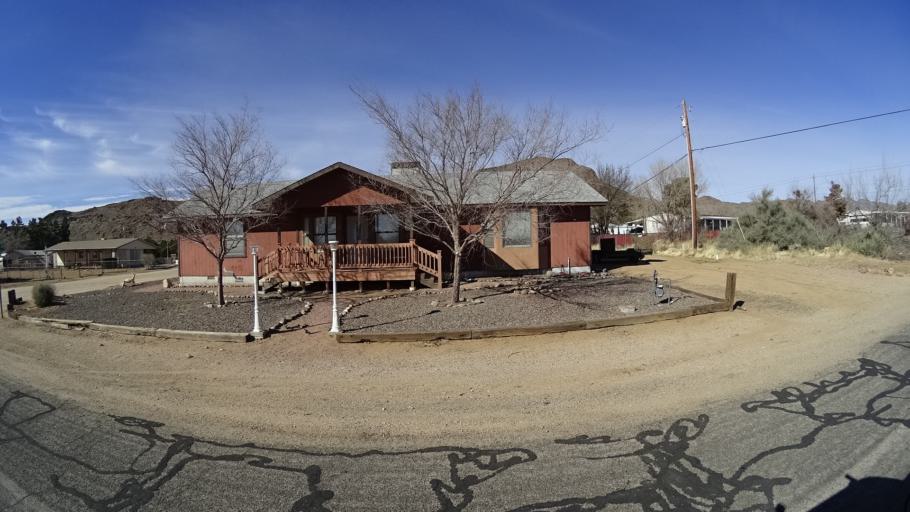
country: US
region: Arizona
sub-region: Mohave County
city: New Kingman-Butler
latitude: 35.2678
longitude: -114.0407
